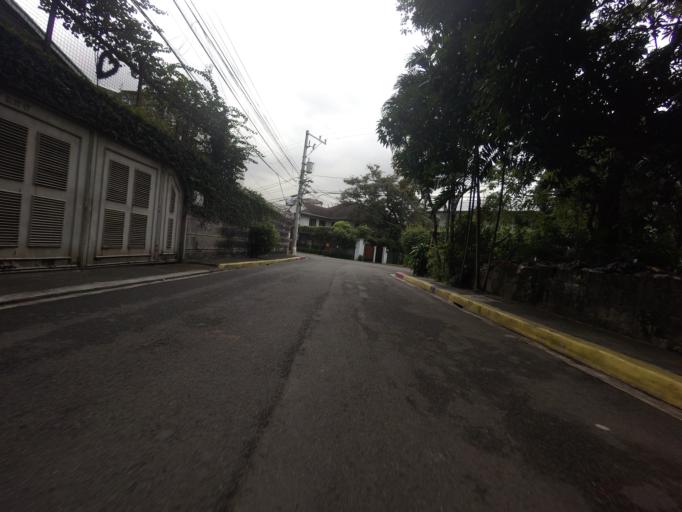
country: PH
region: Metro Manila
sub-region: Mandaluyong
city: Mandaluyong City
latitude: 14.5911
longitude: 121.0437
